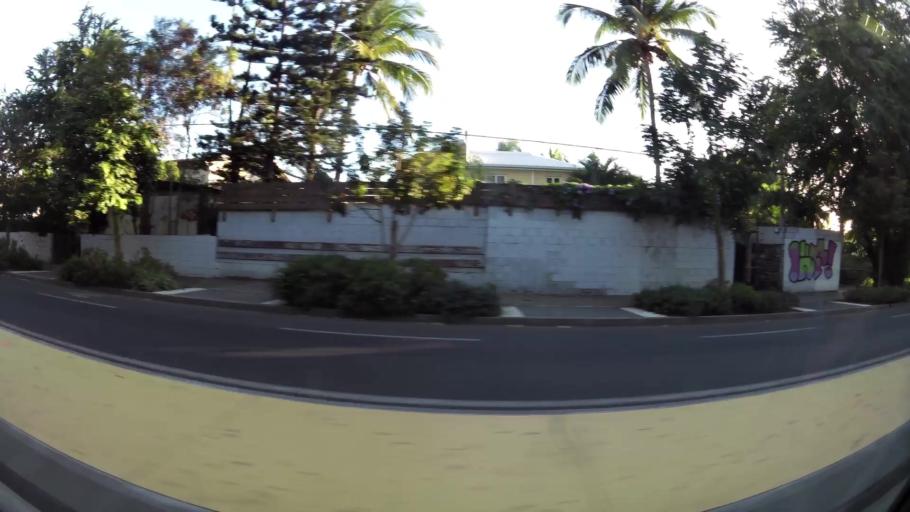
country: RE
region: Reunion
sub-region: Reunion
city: Trois-Bassins
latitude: -21.0824
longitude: 55.2307
